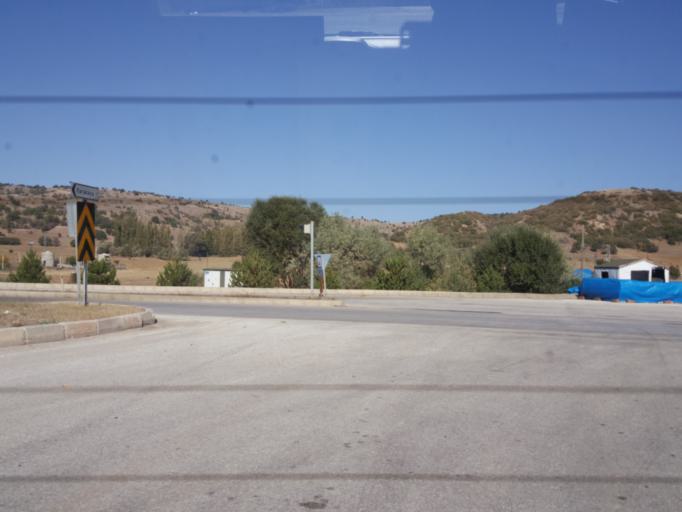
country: TR
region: Corum
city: Alaca
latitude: 40.2595
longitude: 34.6237
